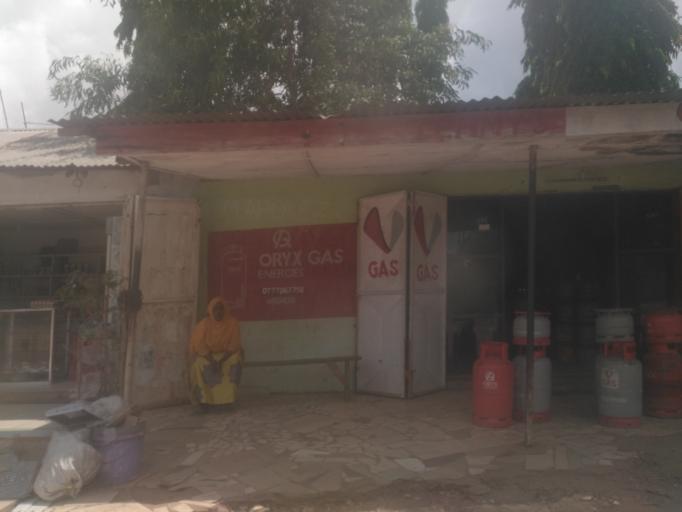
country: TZ
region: Zanzibar Urban/West
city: Zanzibar
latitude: -6.2103
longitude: 39.2108
